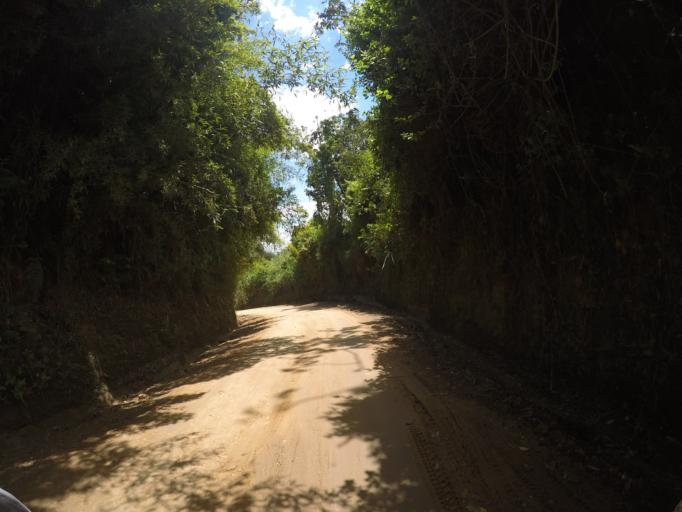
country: CO
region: Valle del Cauca
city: Ulloa
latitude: 4.6979
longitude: -75.7312
